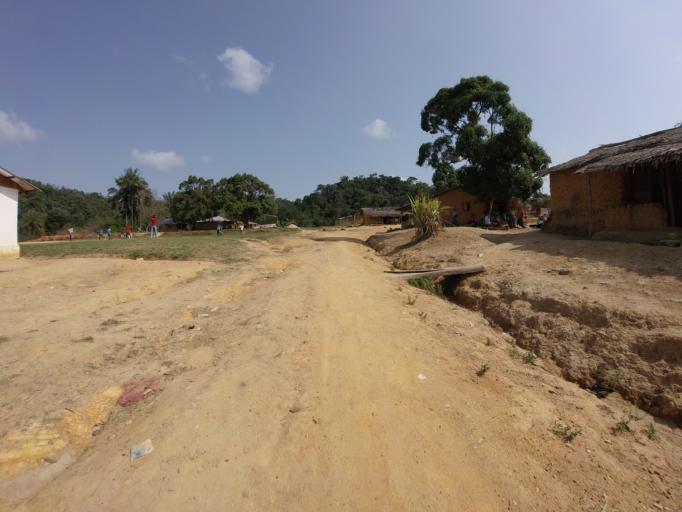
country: SL
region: Eastern Province
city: Jojoima
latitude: 7.6473
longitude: -10.5770
